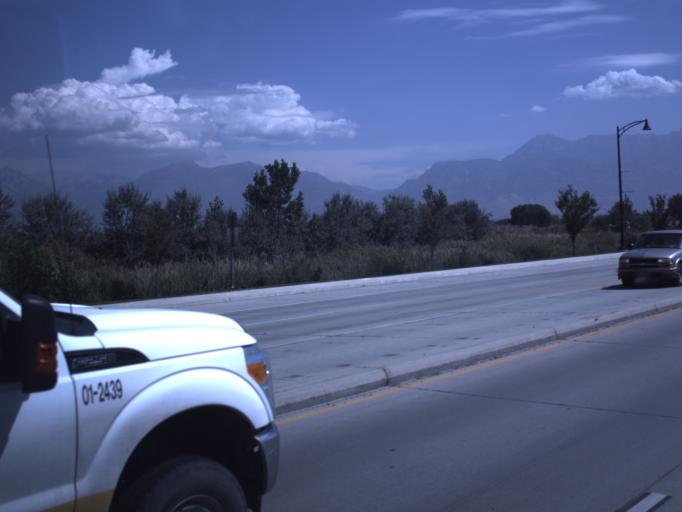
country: US
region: Utah
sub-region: Utah County
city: Saratoga Springs
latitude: 40.3727
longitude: -111.9106
